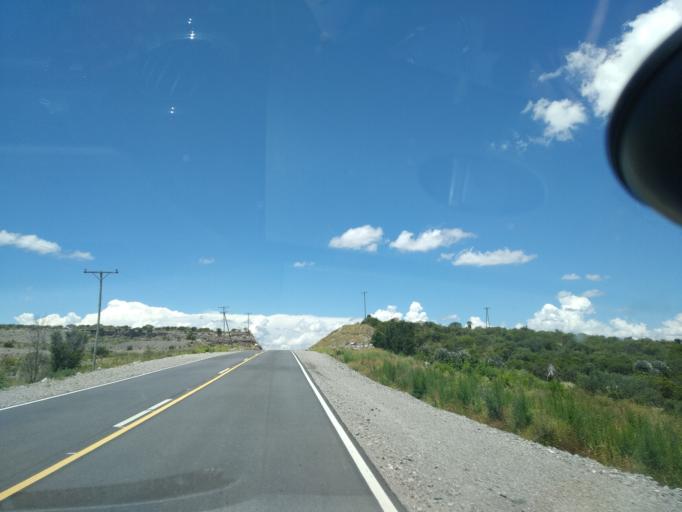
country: AR
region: Cordoba
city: Salsacate
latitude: -31.3639
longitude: -65.2065
